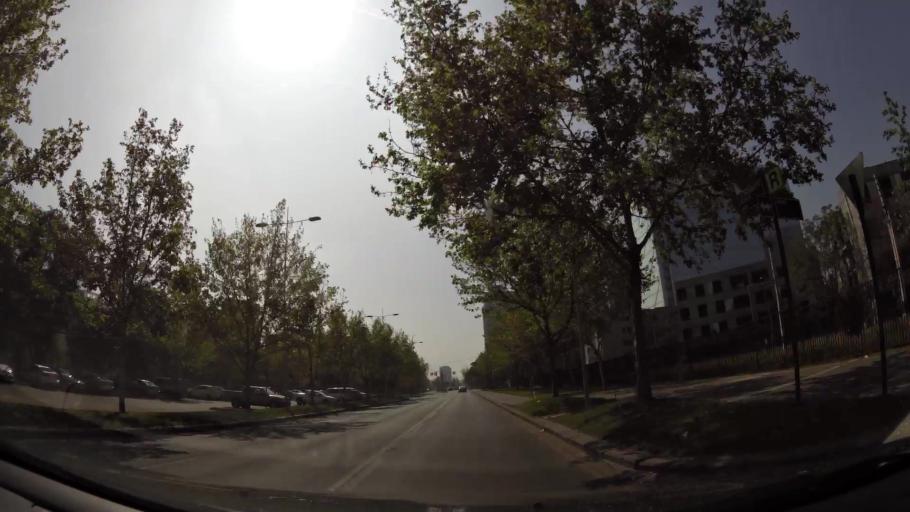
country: CL
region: Santiago Metropolitan
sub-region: Provincia de Santiago
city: Villa Presidente Frei, Nunoa, Santiago, Chile
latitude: -33.4036
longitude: -70.5721
